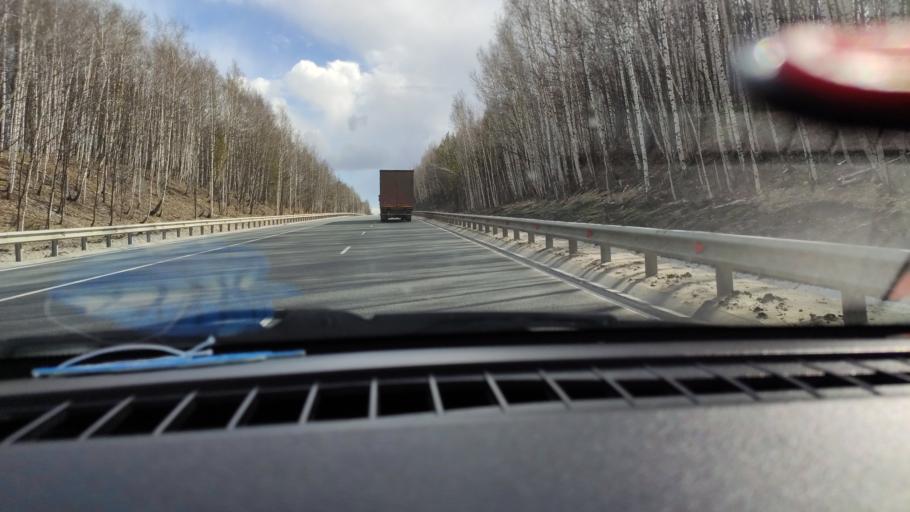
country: RU
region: Saratov
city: Khvalynsk
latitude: 52.5008
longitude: 48.0148
